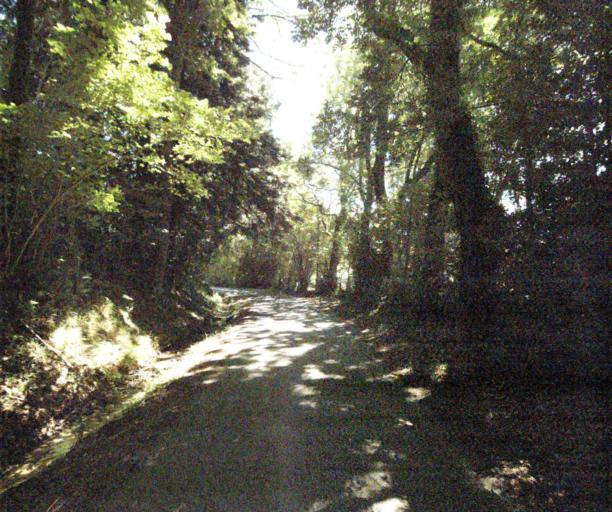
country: FR
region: Midi-Pyrenees
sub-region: Departement du Tarn
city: Dourgne
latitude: 43.4426
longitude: 2.1982
